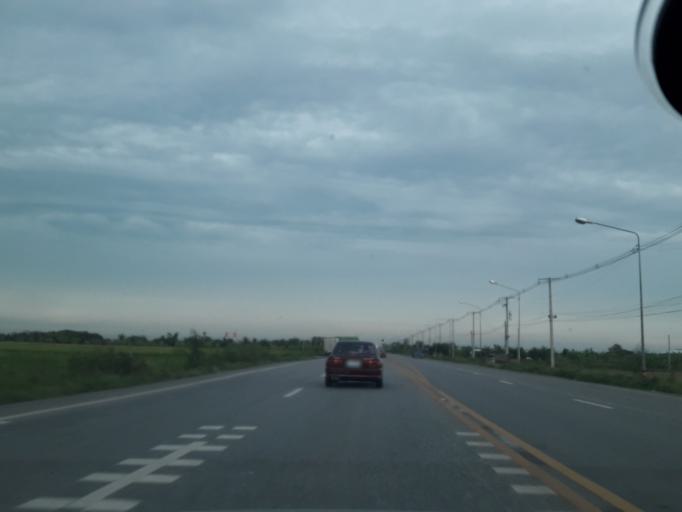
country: TH
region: Pathum Thani
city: Nong Suea
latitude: 14.1396
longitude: 100.7473
